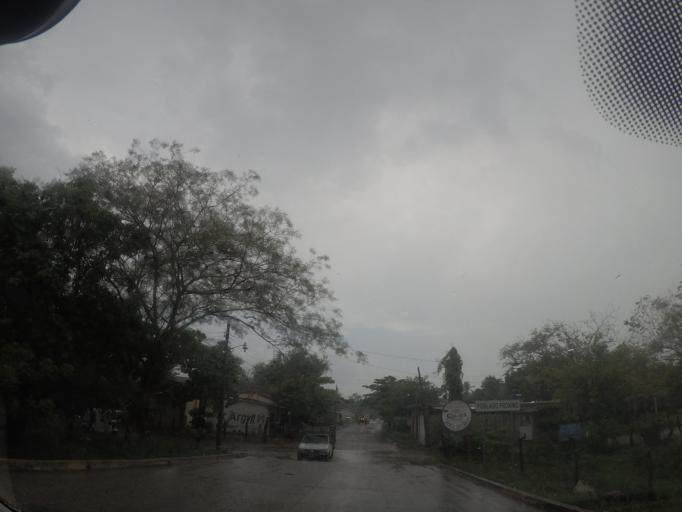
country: MX
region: Oaxaca
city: San Pedro Tapanatepec
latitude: 16.3656
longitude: -94.1967
